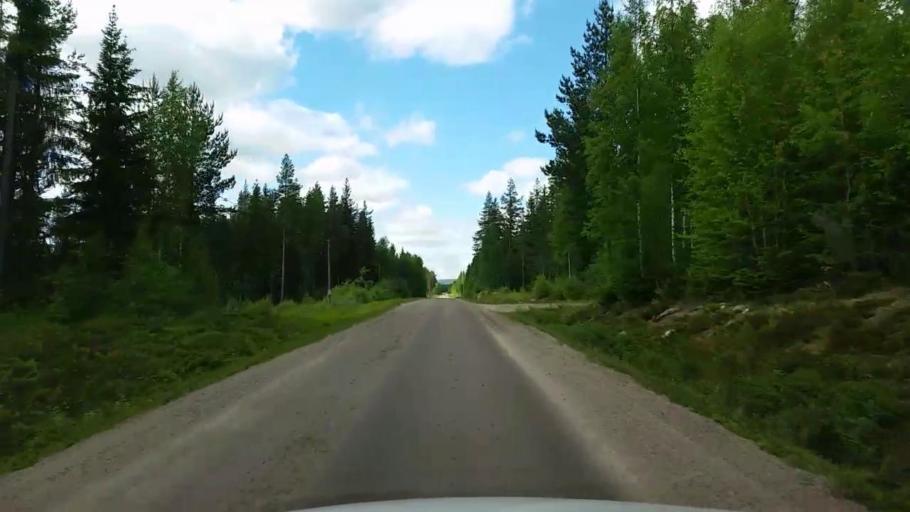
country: SE
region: Gaevleborg
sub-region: Ovanakers Kommun
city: Alfta
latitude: 61.4949
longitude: 15.9804
